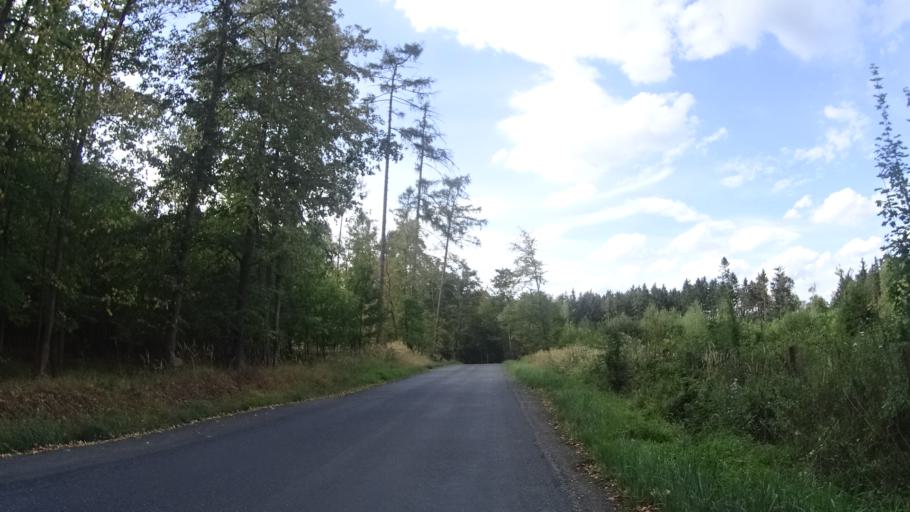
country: CZ
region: Olomoucky
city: Bila Lhota
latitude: 49.7322
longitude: 17.0078
